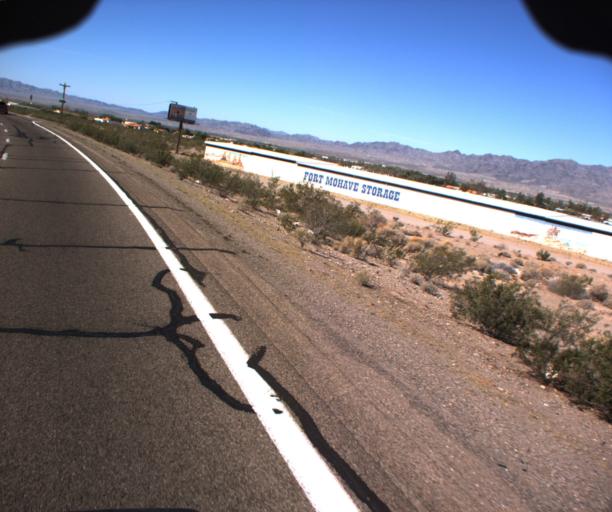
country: US
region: Arizona
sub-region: Mohave County
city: Mohave Valley
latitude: 35.0361
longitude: -114.5972
